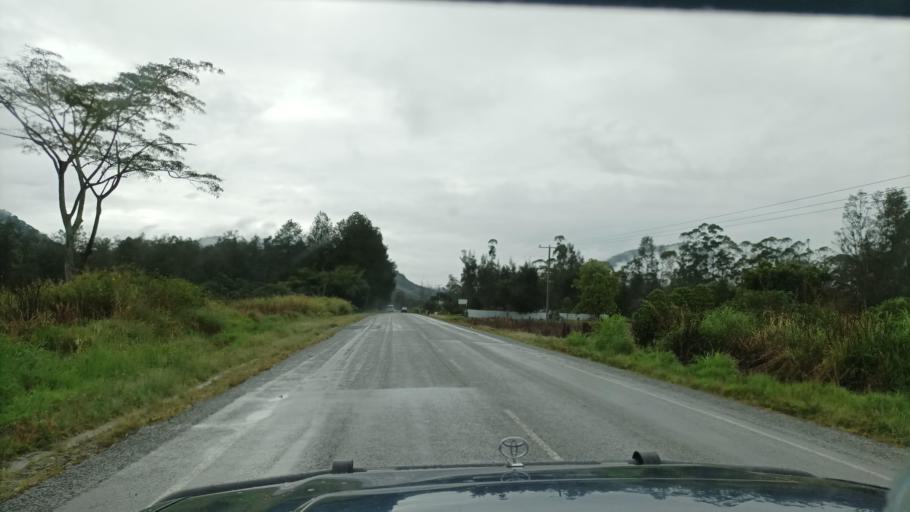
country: PG
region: Western Highlands
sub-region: Hagen
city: Mount Hagen
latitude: -5.8364
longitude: 144.3339
